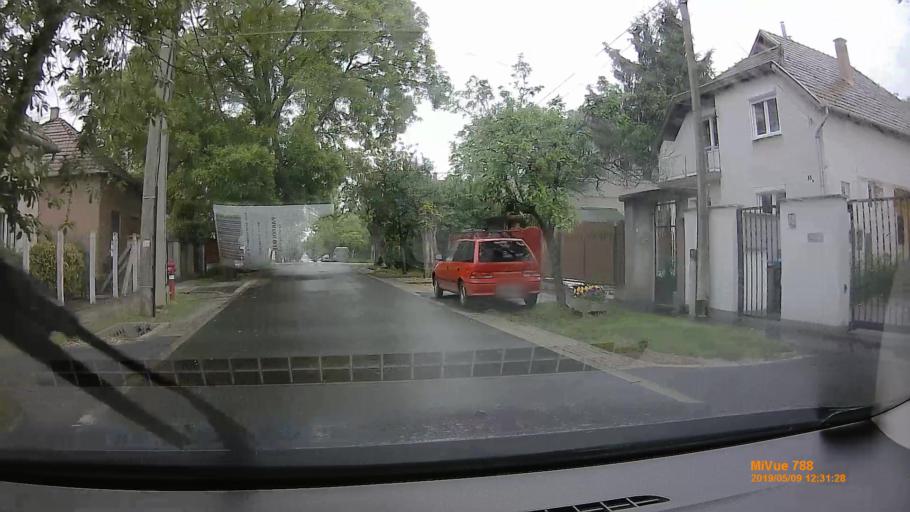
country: HU
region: Budapest
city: Budapest XVI. keruelet
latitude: 47.5225
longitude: 19.1741
